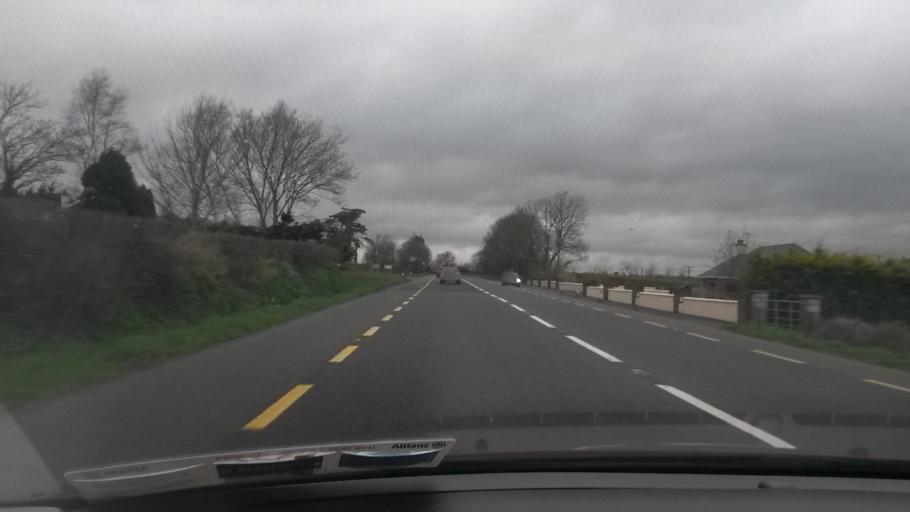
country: IE
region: Munster
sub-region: County Limerick
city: Abbeyfeale
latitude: 52.3865
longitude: -9.2354
